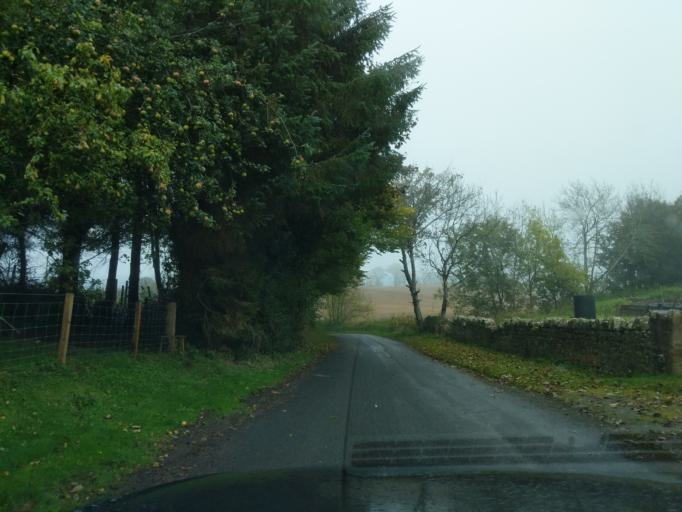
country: GB
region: Scotland
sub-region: East Lothian
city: Dunbar
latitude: 55.9454
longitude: -2.4230
